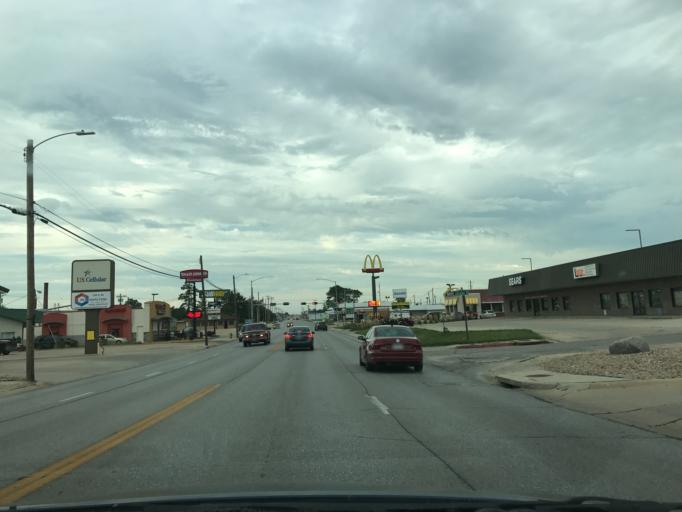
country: US
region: Nebraska
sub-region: Gage County
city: Beatrice
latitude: 40.2776
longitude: -96.7466
